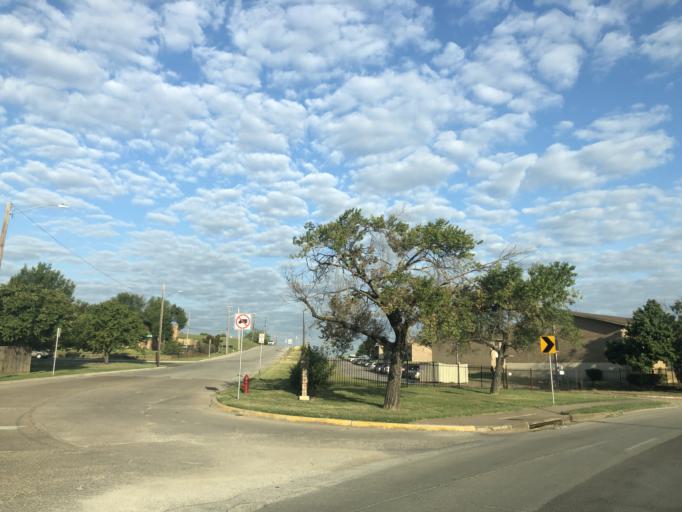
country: US
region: Texas
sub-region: Dallas County
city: Grand Prairie
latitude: 32.7561
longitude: -97.0080
